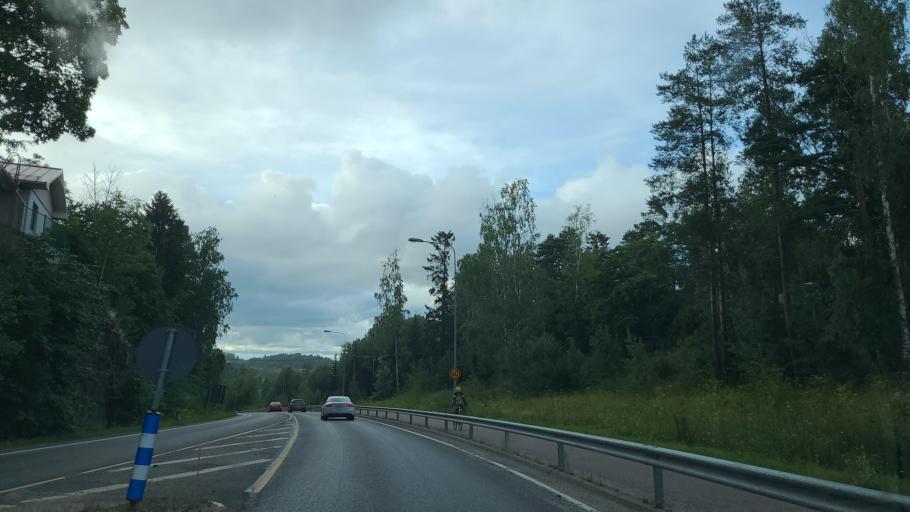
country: FI
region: Varsinais-Suomi
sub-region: Turku
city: Kaarina
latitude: 60.3934
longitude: 22.3948
